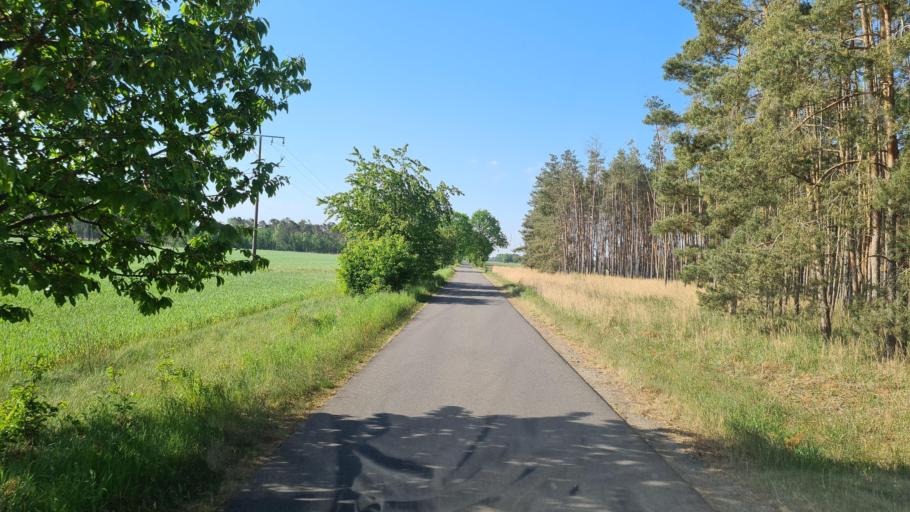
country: DE
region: Brandenburg
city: Falkenberg
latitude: 51.6070
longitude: 13.2045
